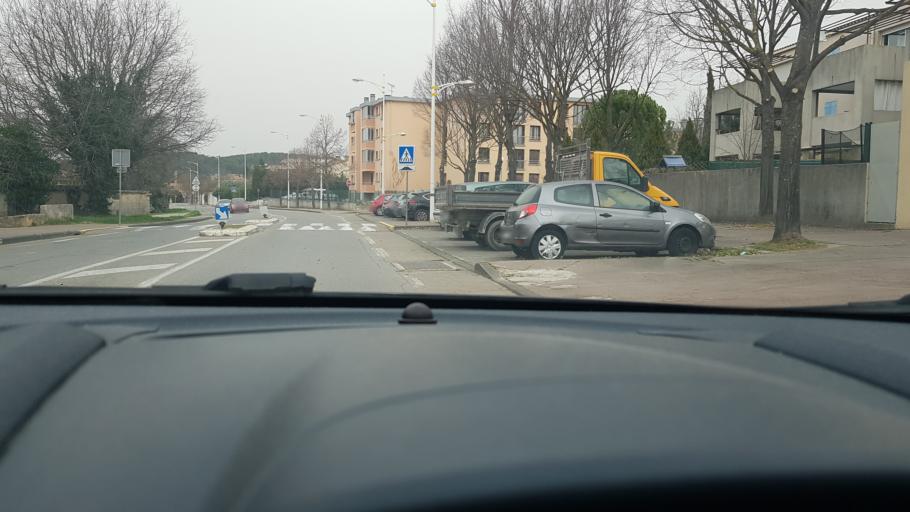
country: FR
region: Provence-Alpes-Cote d'Azur
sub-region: Departement des Bouches-du-Rhone
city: Gardanne
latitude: 43.4486
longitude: 5.4729
